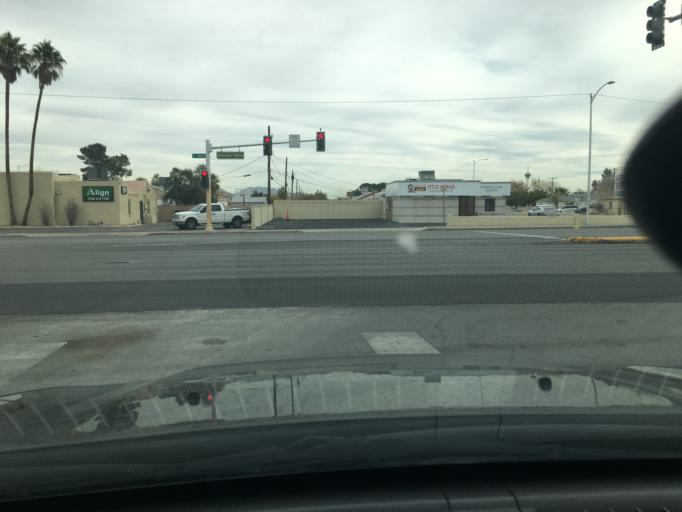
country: US
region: Nevada
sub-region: Clark County
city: Spring Valley
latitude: 36.1630
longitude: -115.2063
